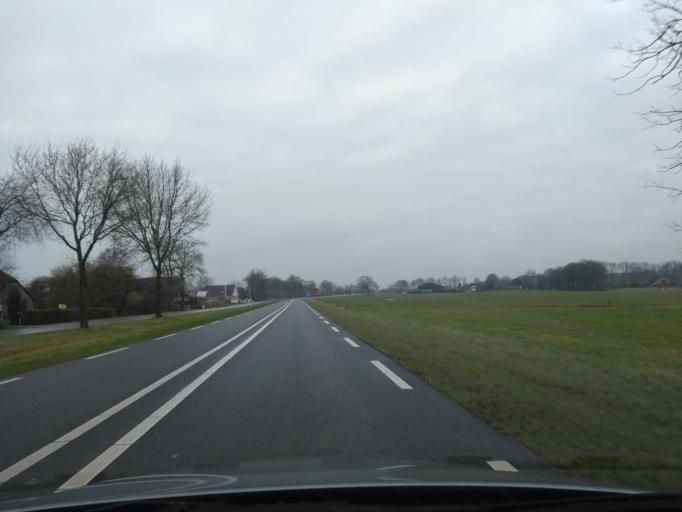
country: NL
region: Overijssel
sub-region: Gemeente Steenwijkerland
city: Sint Jansklooster
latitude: 52.6607
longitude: 5.9974
